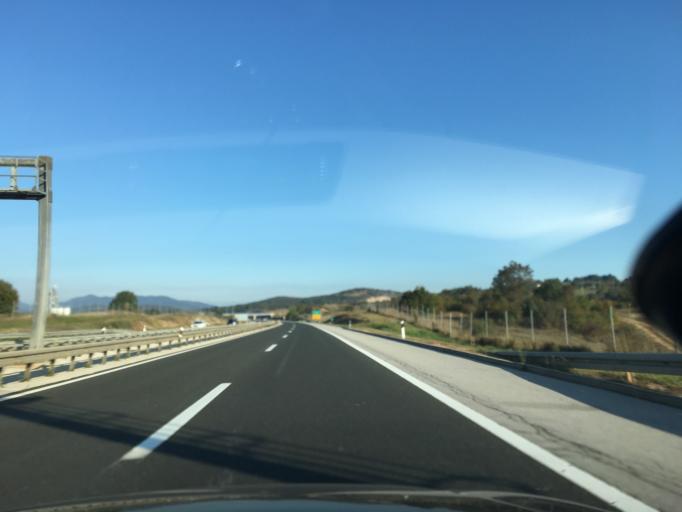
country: HR
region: Licko-Senjska
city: Gospic
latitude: 44.6618
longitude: 15.4250
